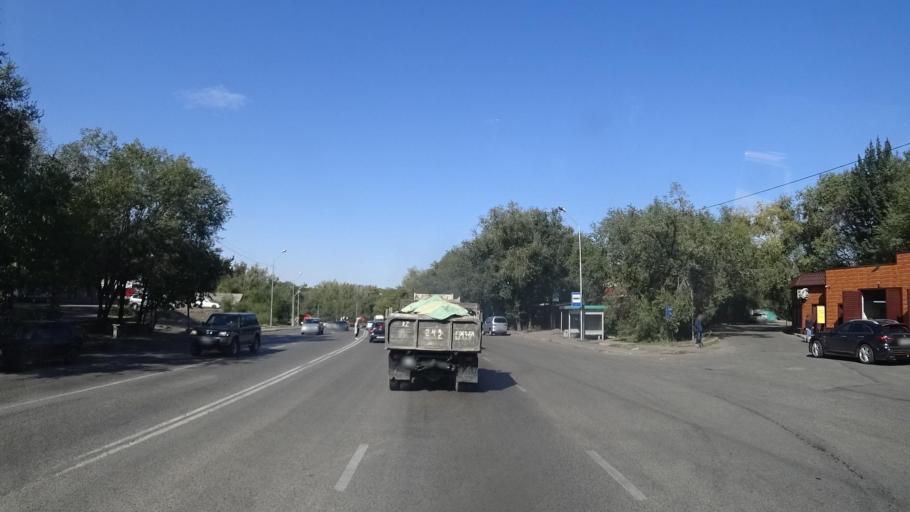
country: KZ
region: Almaty Oblysy
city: Pervomayskiy
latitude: 43.3550
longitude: 76.9479
